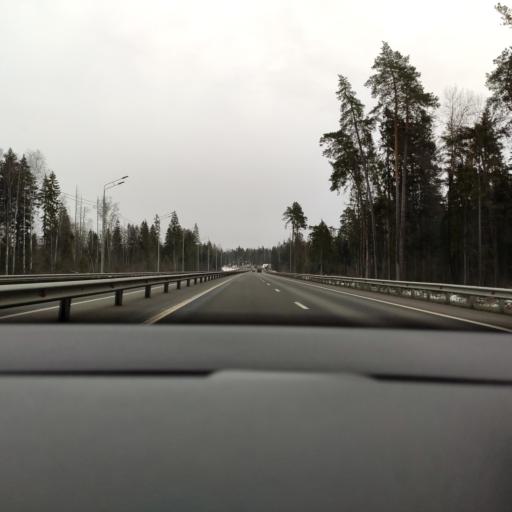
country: RU
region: Moskovskaya
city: Bol'shiye Vyazemy
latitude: 55.6605
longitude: 36.9567
